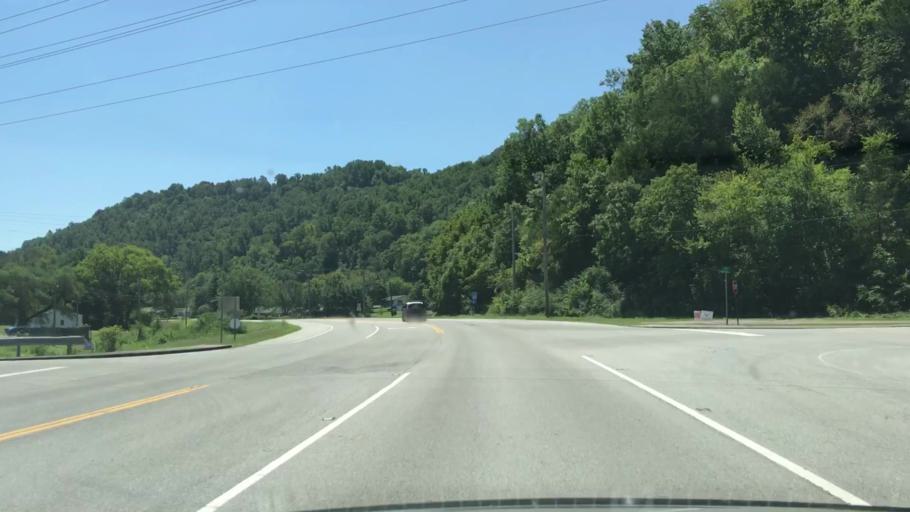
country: US
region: Tennessee
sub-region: Jackson County
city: Gainesboro
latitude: 36.3492
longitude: -85.6577
